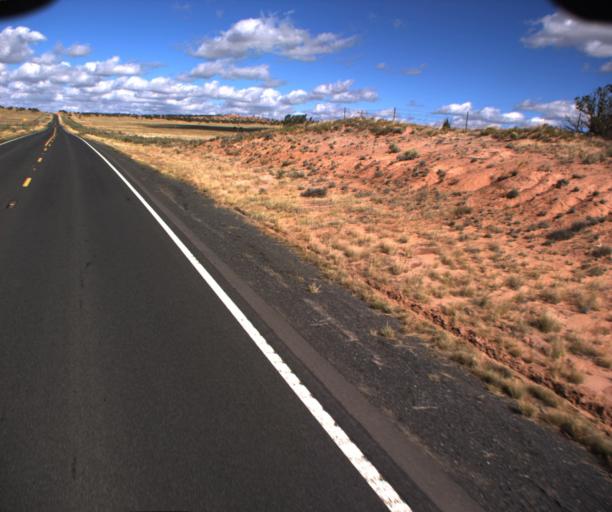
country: US
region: Arizona
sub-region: Apache County
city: Houck
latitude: 35.0595
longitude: -109.2788
